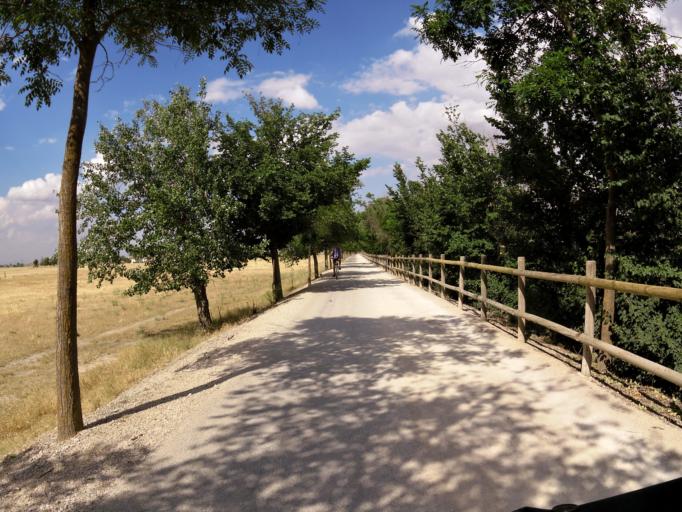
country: ES
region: Castille-La Mancha
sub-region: Provincia de Albacete
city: Albacete
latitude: 38.9904
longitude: -1.9094
